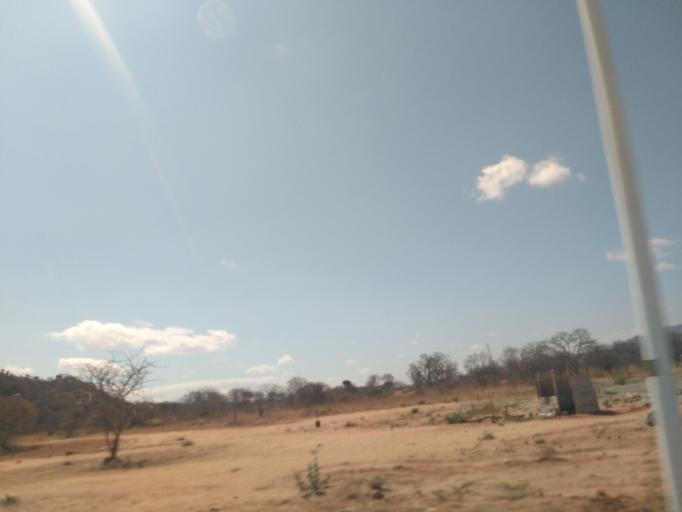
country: TZ
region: Dodoma
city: Dodoma
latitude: -6.1563
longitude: 35.7579
